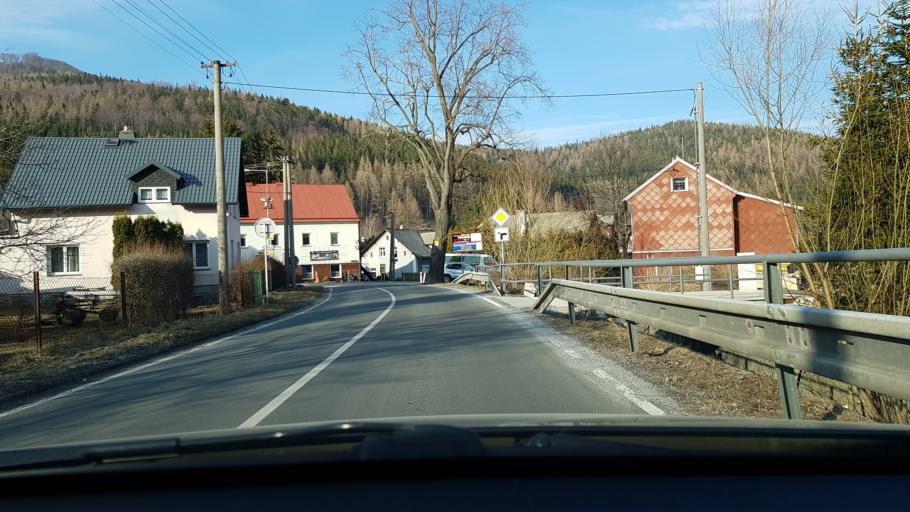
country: CZ
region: Olomoucky
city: Vapenna
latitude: 50.2219
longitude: 17.1073
